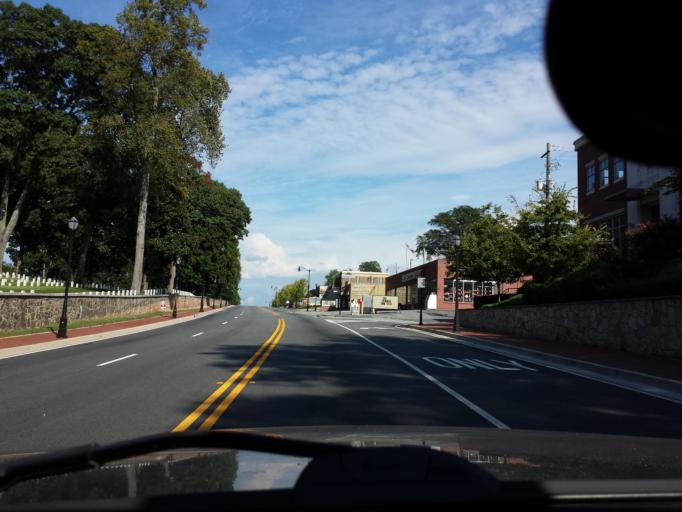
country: US
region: Georgia
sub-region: Cobb County
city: Marietta
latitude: 33.9503
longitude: -84.5423
